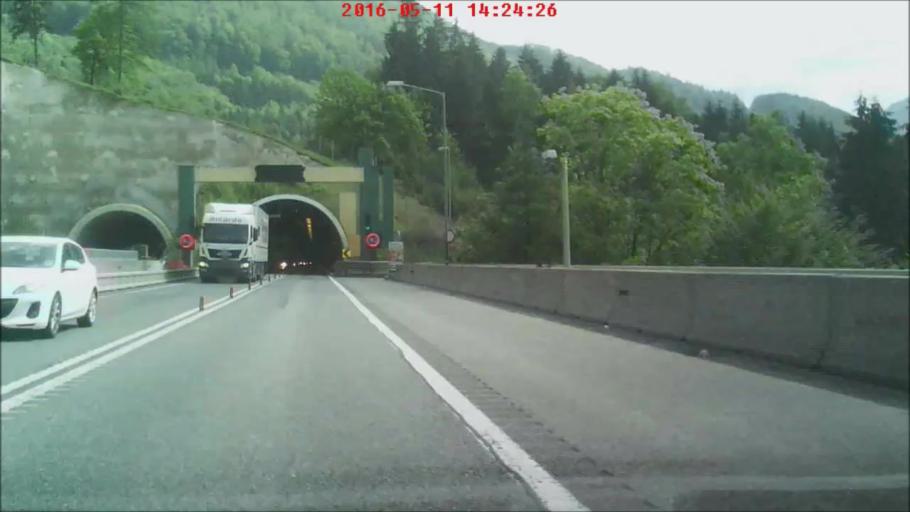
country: AT
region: Upper Austria
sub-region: Politischer Bezirk Kirchdorf an der Krems
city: Micheldorf in Oberoesterreich
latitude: 47.8403
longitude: 14.1705
